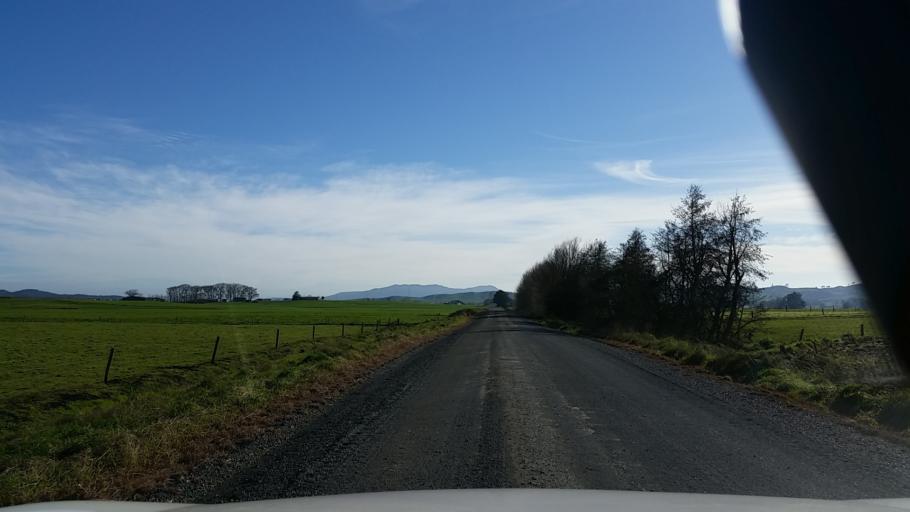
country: NZ
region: Waikato
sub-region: Hamilton City
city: Hamilton
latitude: -37.6295
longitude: 175.4280
